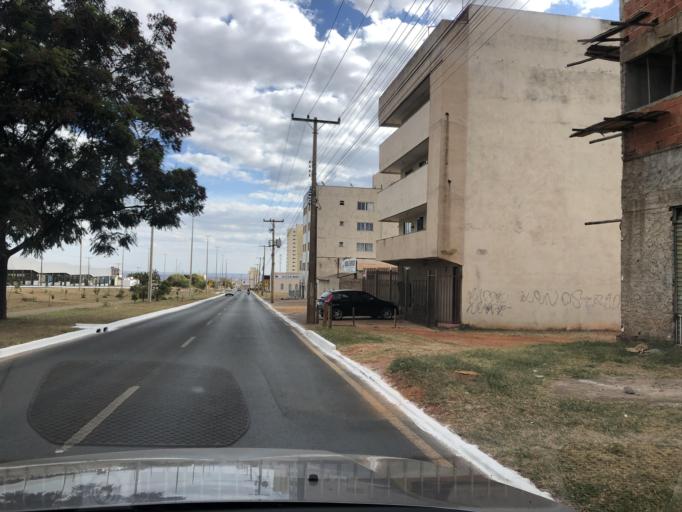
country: BR
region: Federal District
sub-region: Brasilia
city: Brasilia
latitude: -15.8858
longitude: -48.1043
